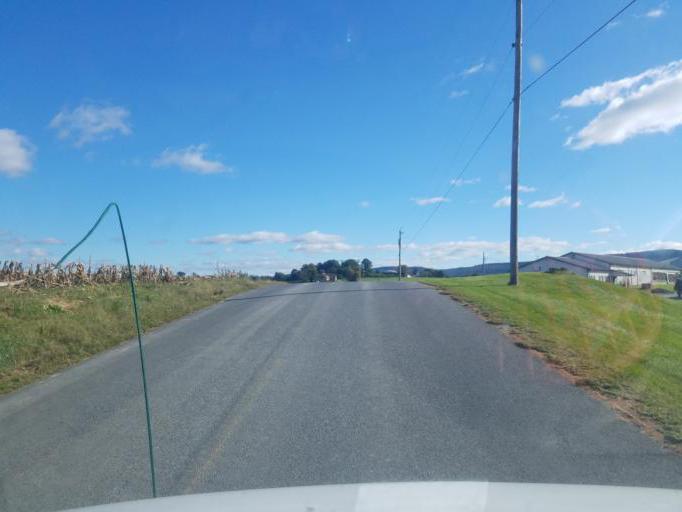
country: US
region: Pennsylvania
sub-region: Franklin County
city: Guilford Siding
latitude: 39.8099
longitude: -77.6039
